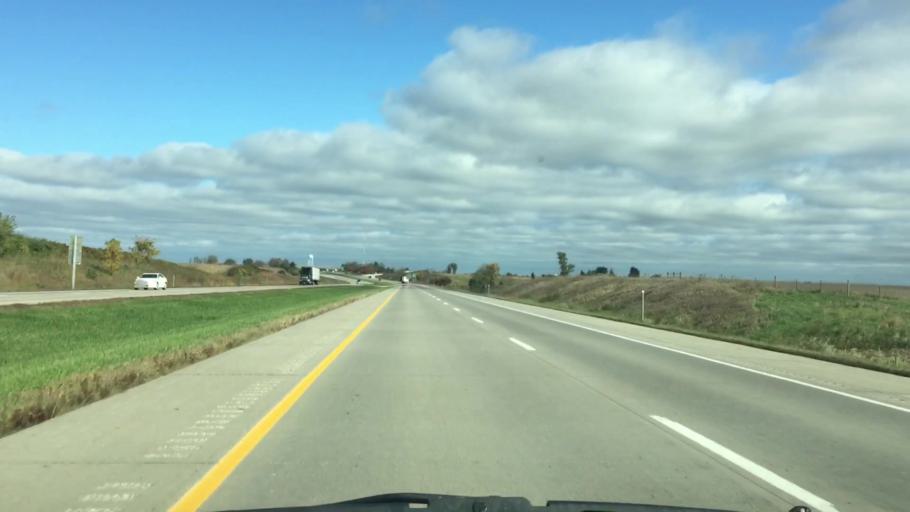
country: US
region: Iowa
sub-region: Clarke County
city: Osceola
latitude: 40.9608
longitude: -93.7980
